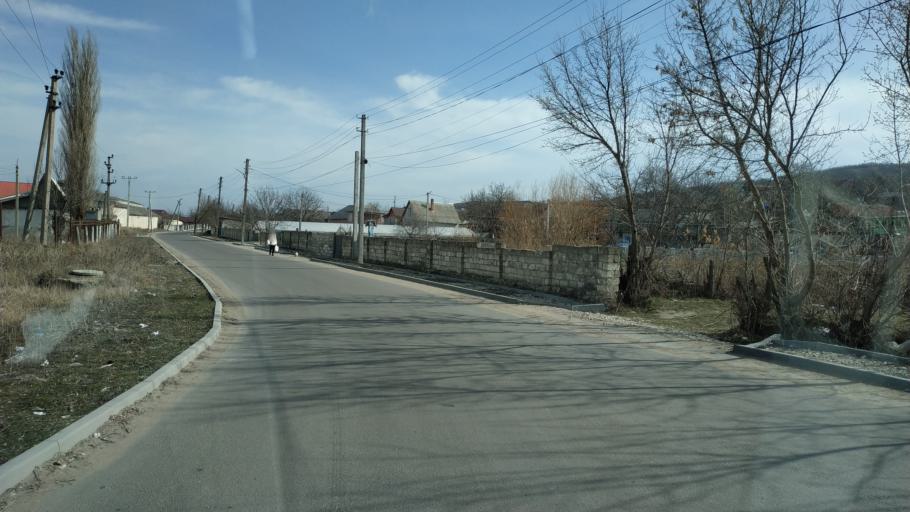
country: MD
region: Straseni
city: Straseni
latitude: 47.0930
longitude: 28.6561
